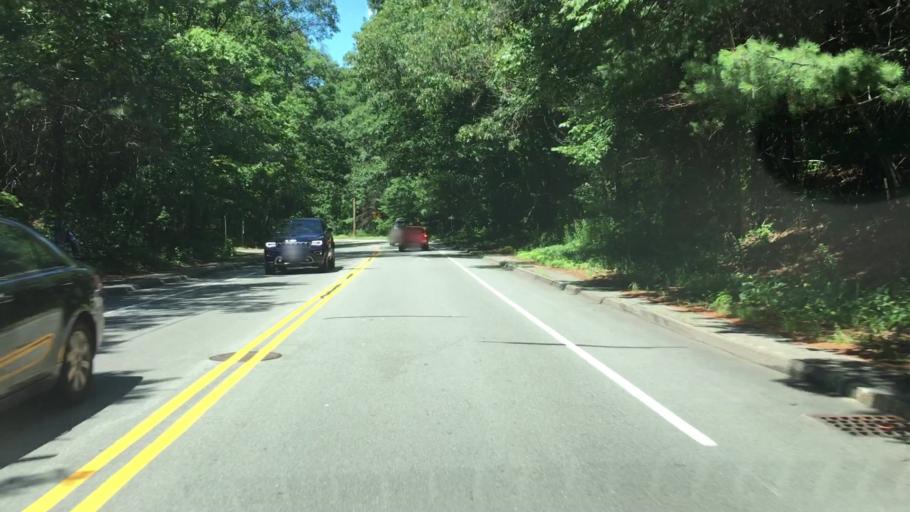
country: US
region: Massachusetts
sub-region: Middlesex County
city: Lexington
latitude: 42.4462
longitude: -71.2607
